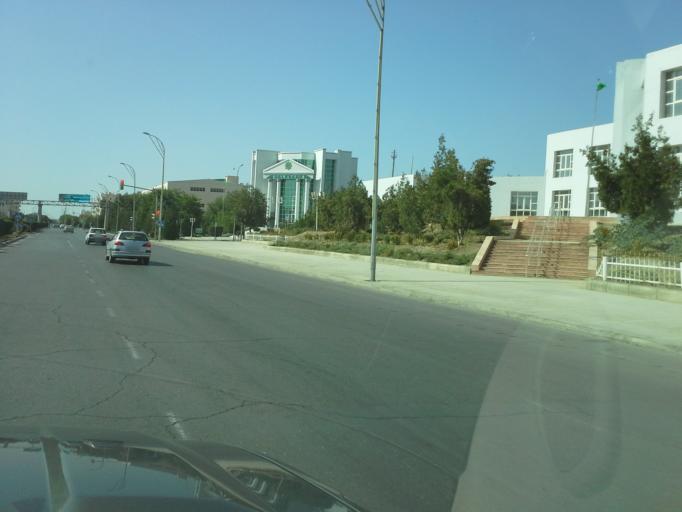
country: TM
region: Dasoguz
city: Dasoguz
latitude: 41.8355
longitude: 59.9622
